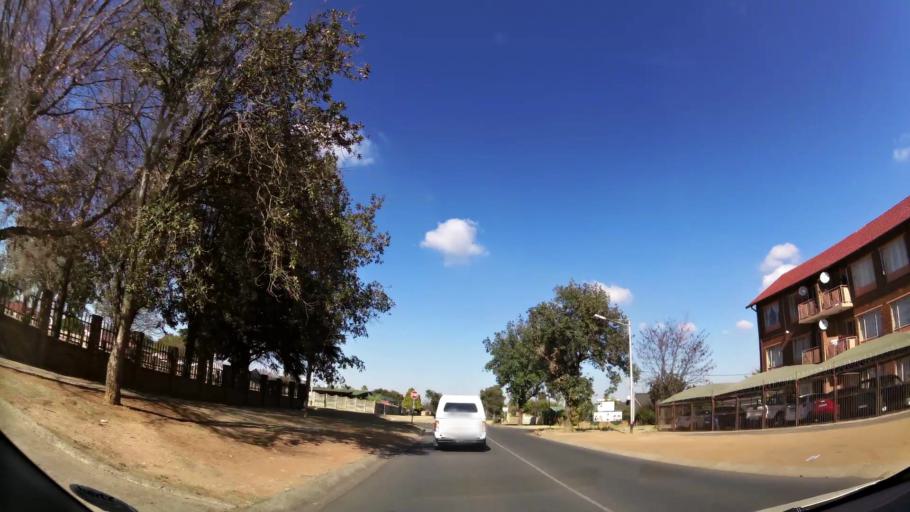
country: ZA
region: Gauteng
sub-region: City of Johannesburg Metropolitan Municipality
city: Roodepoort
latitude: -26.1418
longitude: 27.8300
